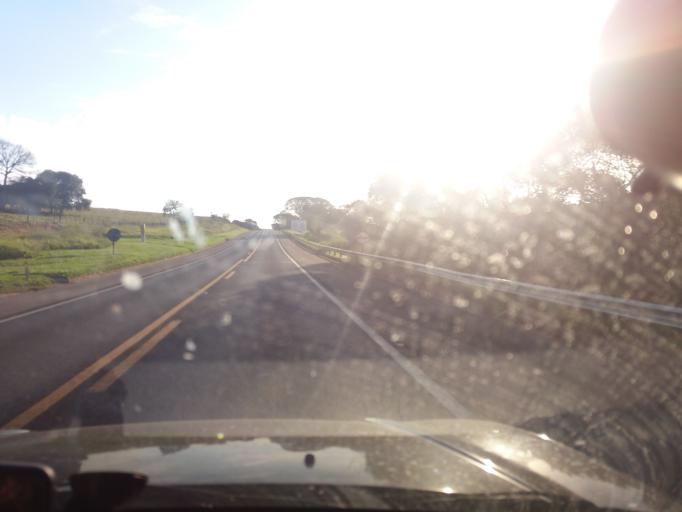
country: BR
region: Sao Paulo
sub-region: Buri
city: Buri
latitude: -23.9310
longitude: -48.6426
